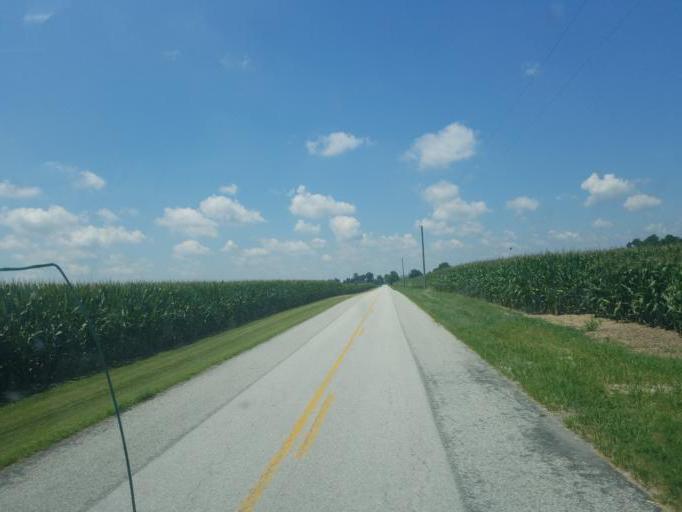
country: US
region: Ohio
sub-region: Allen County
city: Spencerville
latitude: 40.6666
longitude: -84.4209
